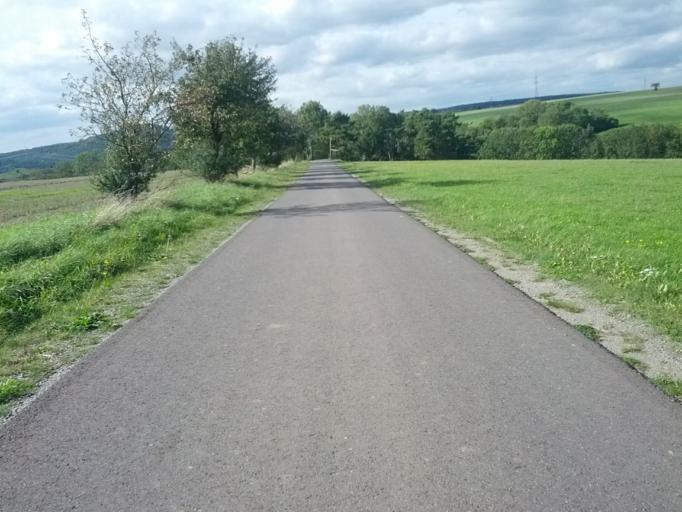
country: DE
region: Thuringia
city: Eisenach
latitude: 51.0193
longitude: 10.3189
